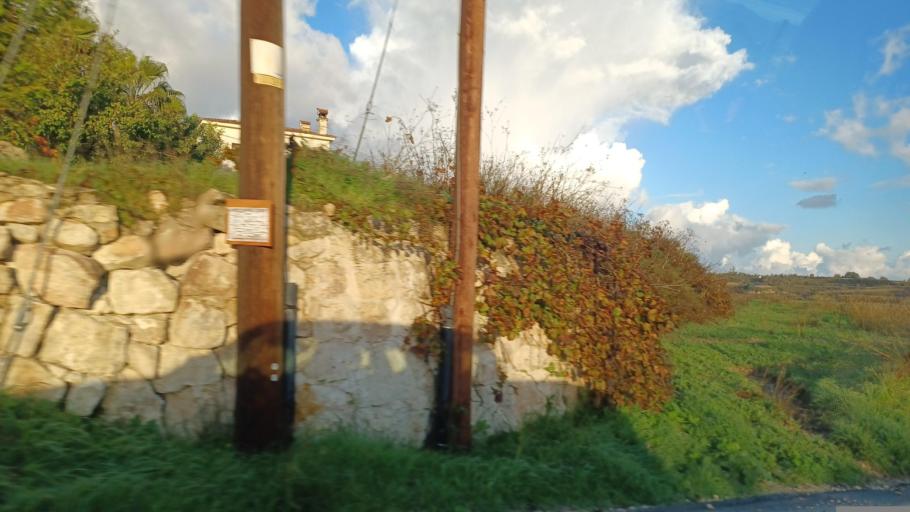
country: CY
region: Pafos
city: Mesogi
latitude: 34.8679
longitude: 32.5038
